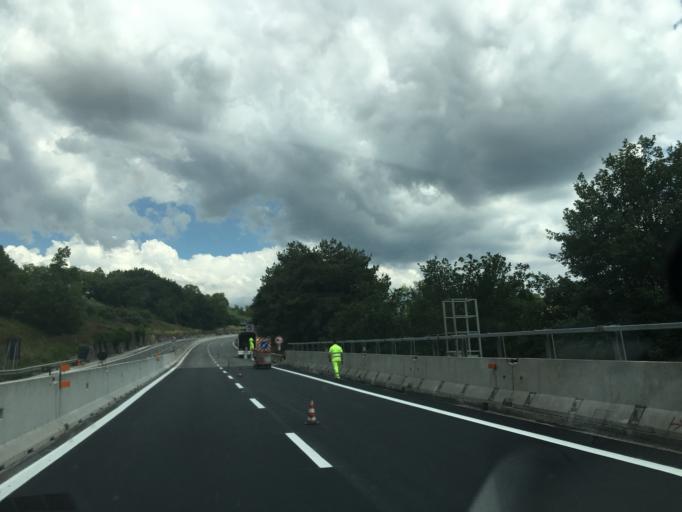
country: IT
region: Campania
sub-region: Provincia di Avellino
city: Campanarello
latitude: 41.0736
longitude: 14.9398
